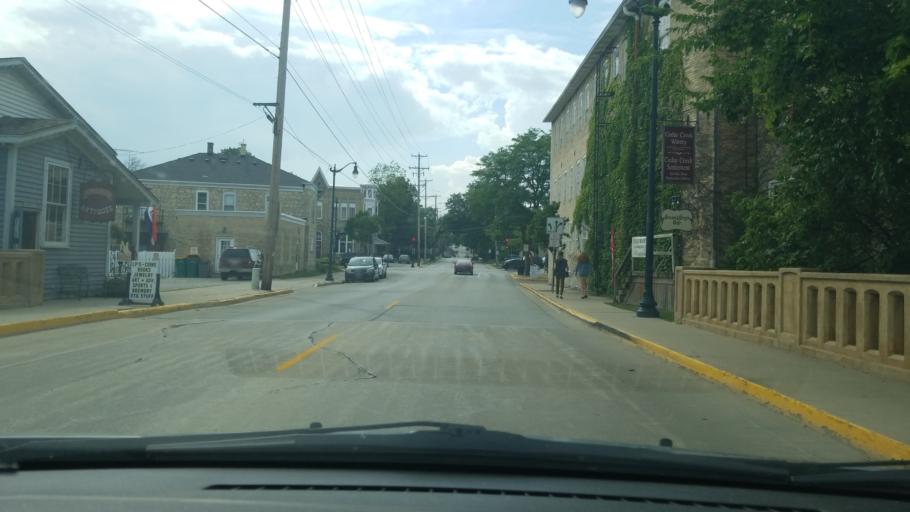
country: US
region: Wisconsin
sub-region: Ozaukee County
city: Cedarburg
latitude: 43.3011
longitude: -87.9882
